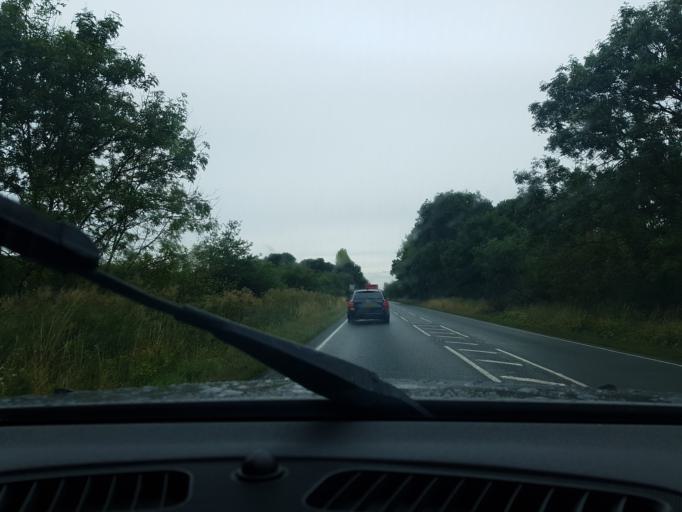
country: GB
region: England
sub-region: Hampshire
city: Fleet
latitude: 51.2458
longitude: -0.8647
